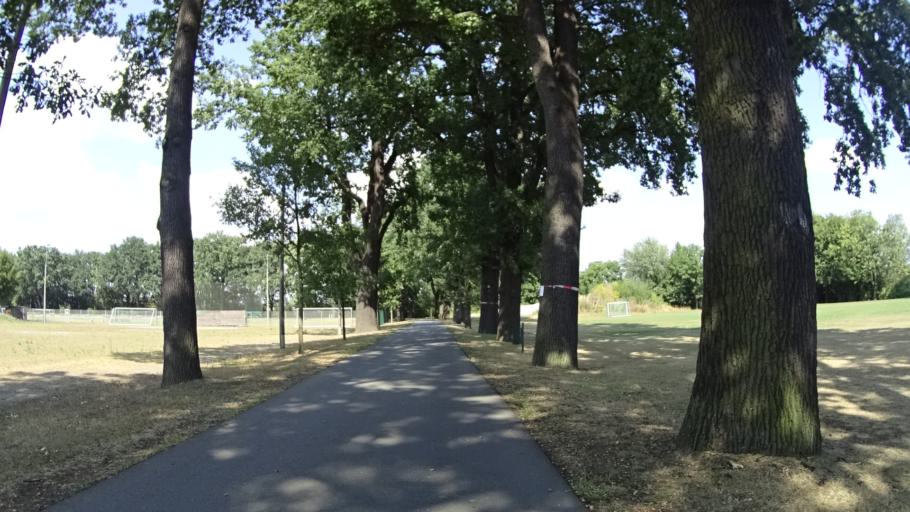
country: DE
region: Saxony
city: Zittau
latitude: 50.9005
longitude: 14.8396
